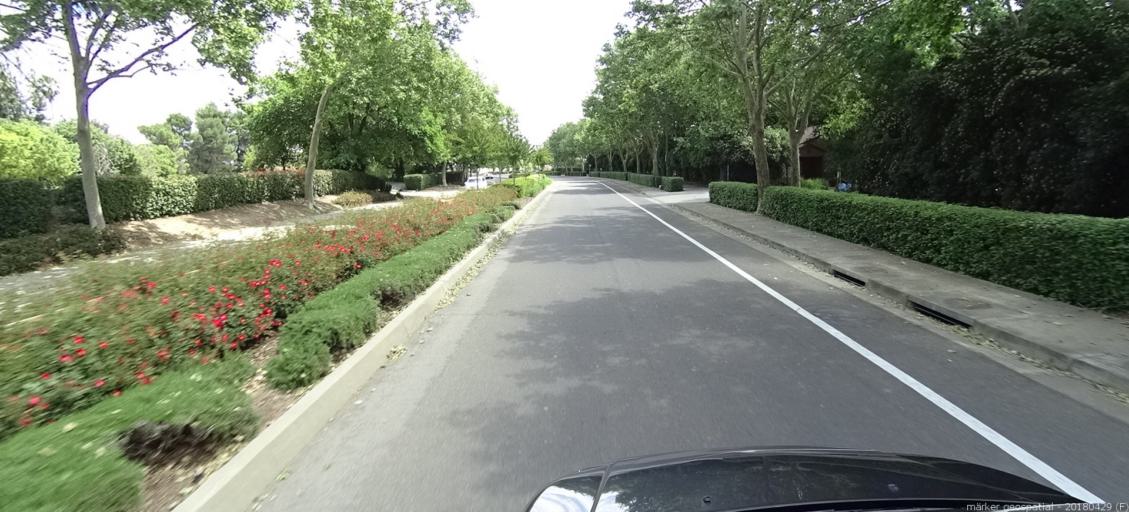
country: US
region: California
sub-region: Yolo County
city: West Sacramento
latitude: 38.5953
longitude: -121.5175
